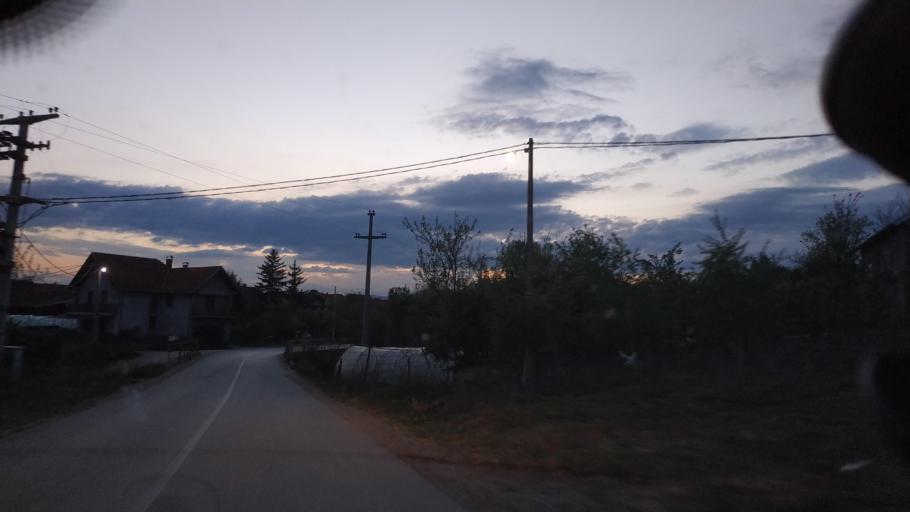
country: RS
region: Central Serbia
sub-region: Nisavski Okrug
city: Merosina
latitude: 43.2993
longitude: 21.7008
